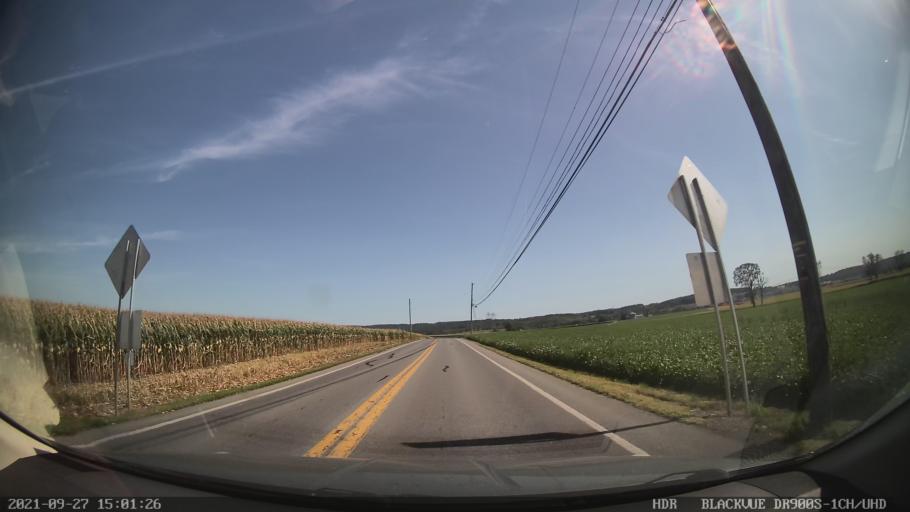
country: US
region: Pennsylvania
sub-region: Berks County
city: Kutztown
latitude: 40.4948
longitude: -75.7631
